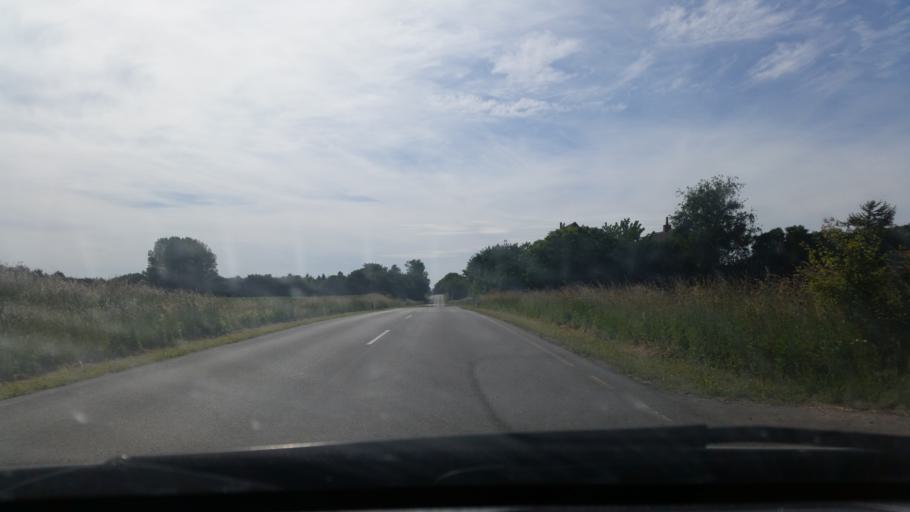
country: DK
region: Central Jutland
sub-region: Samso Kommune
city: Tranebjerg
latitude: 55.8000
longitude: 10.5438
